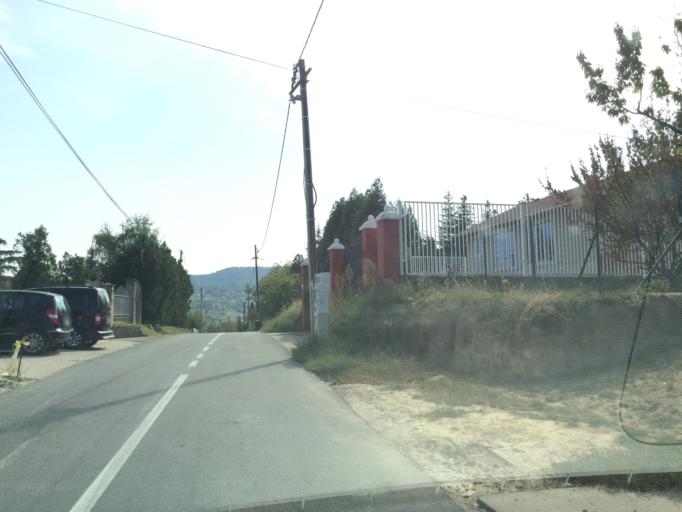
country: RS
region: Autonomna Pokrajina Vojvodina
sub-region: Juznobacki Okrug
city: Novi Sad
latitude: 45.2020
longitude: 19.8325
